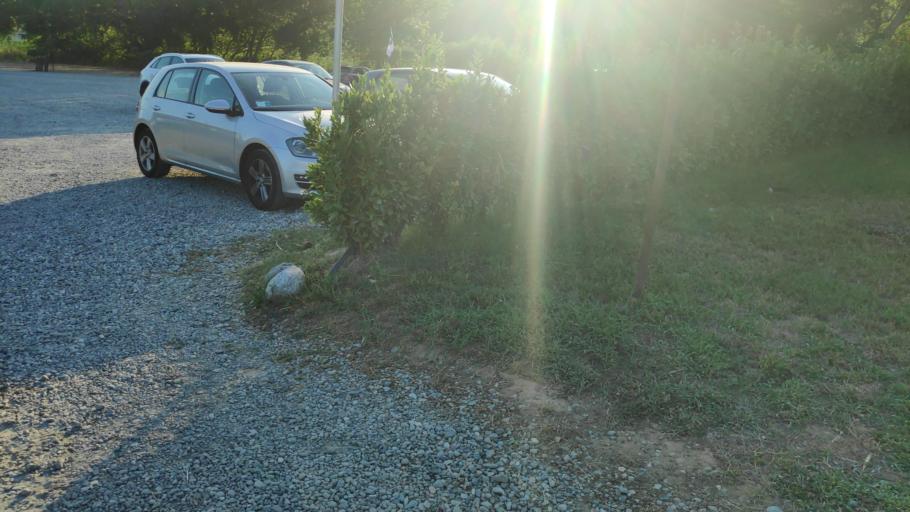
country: IT
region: Calabria
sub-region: Provincia di Catanzaro
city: San Floro
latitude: 38.8503
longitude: 16.5323
